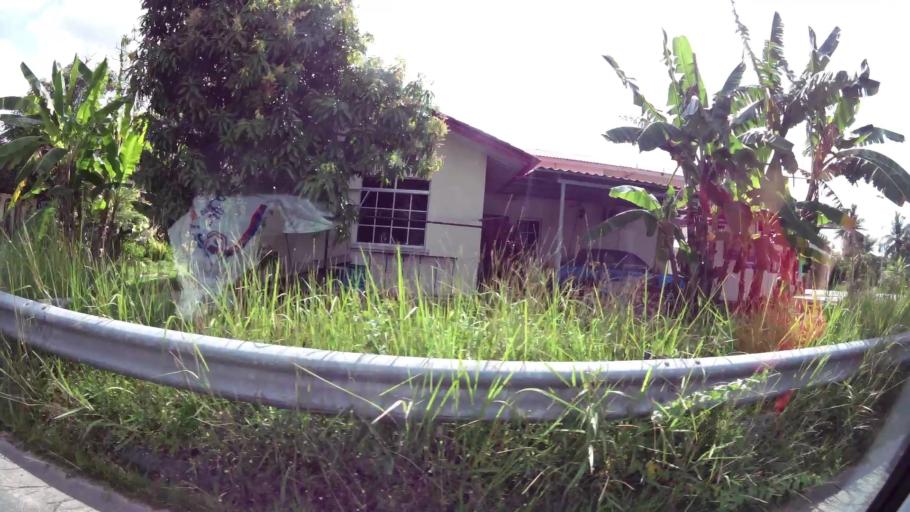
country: BN
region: Brunei and Muara
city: Bandar Seri Begawan
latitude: 4.9624
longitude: 114.9564
